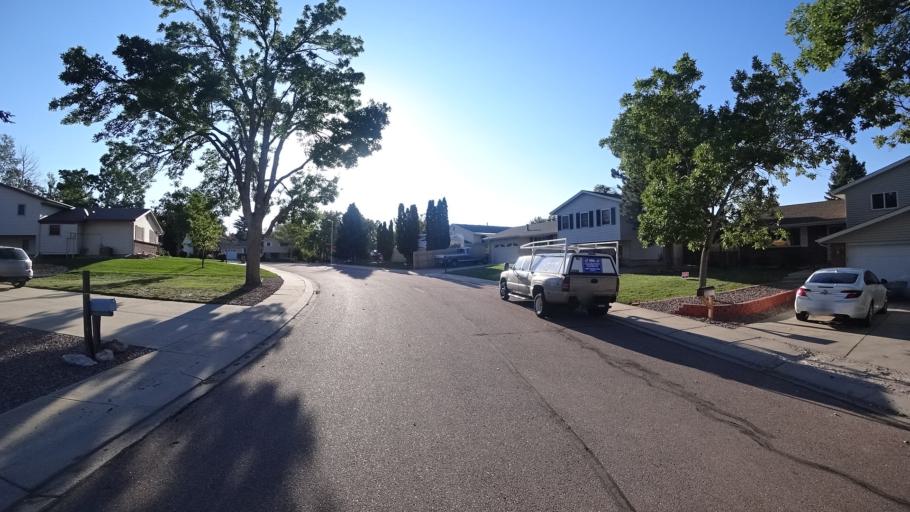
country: US
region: Colorado
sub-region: El Paso County
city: Cimarron Hills
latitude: 38.8814
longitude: -104.7475
